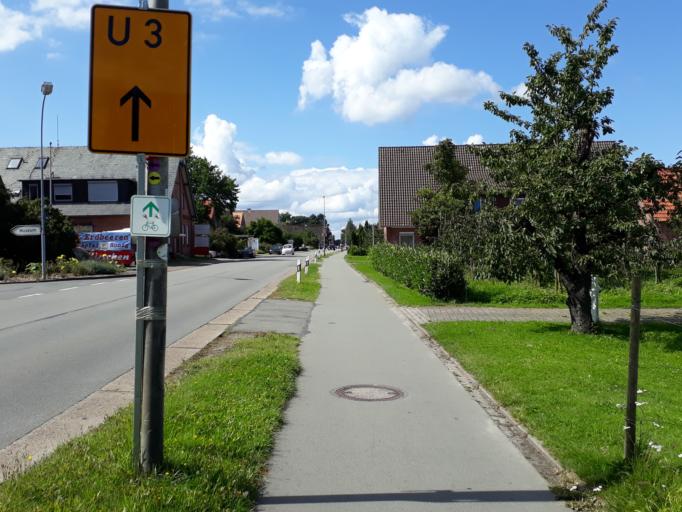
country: DE
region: Lower Saxony
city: Jork
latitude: 53.5348
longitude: 9.6723
